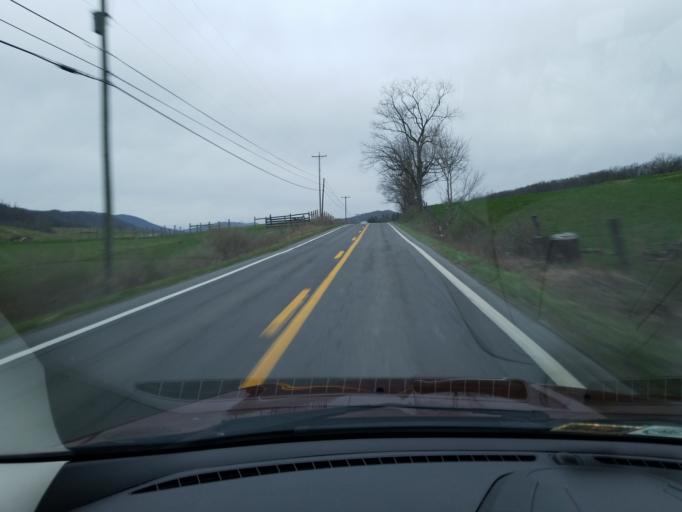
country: US
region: Virginia
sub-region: Giles County
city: Pearisburg
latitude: 37.4270
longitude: -80.7244
